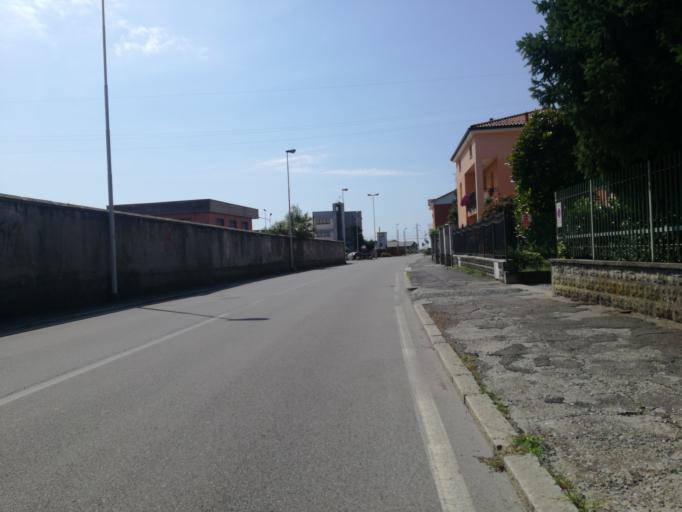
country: IT
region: Lombardy
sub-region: Provincia di Bergamo
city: Calusco d'Adda
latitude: 45.6858
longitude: 9.4729
